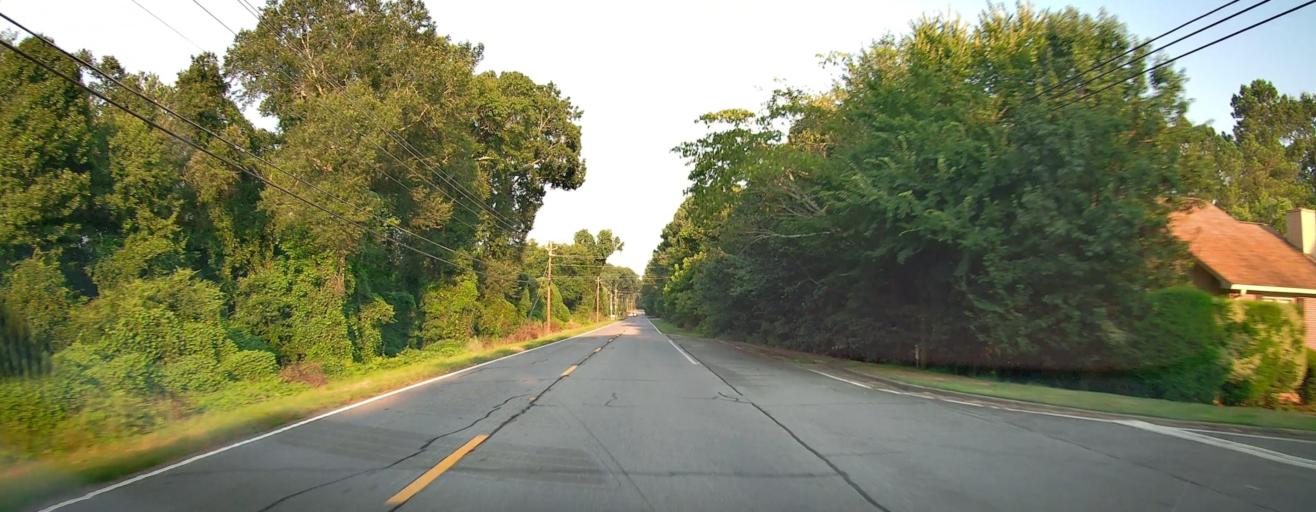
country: US
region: Georgia
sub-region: Bibb County
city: West Point
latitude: 32.8872
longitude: -83.7399
